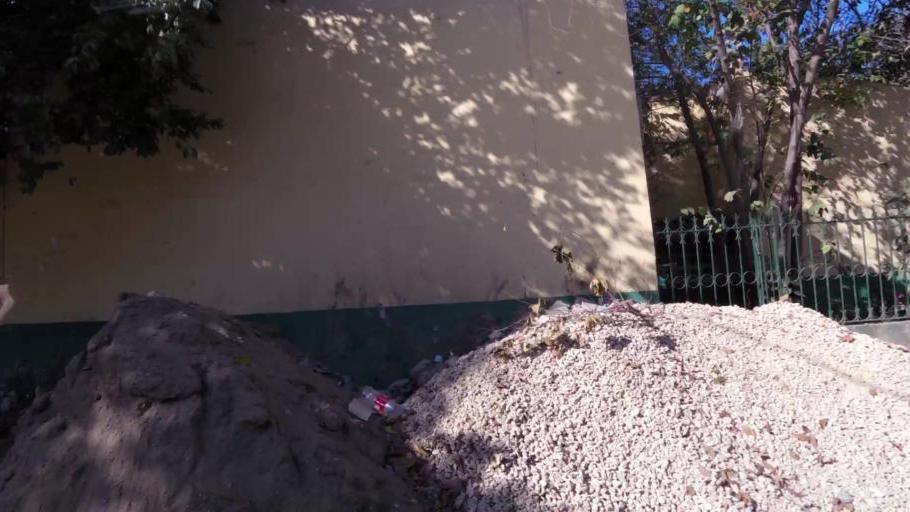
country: CO
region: Bolivar
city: Cartagena
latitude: 10.3792
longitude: -75.4764
